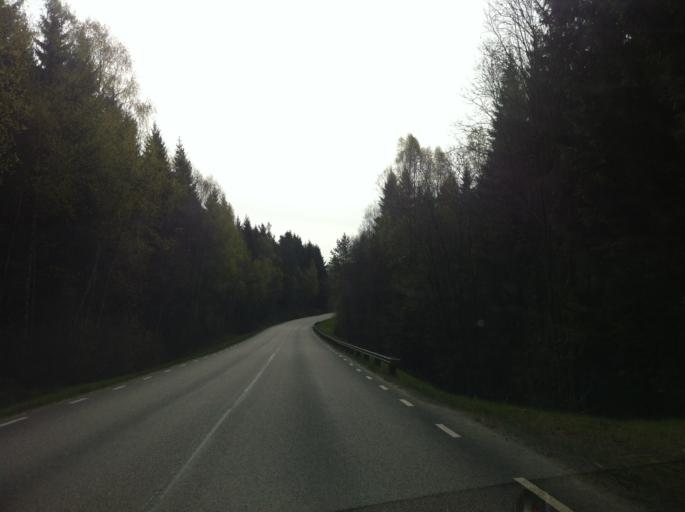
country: SE
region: Vaestra Goetaland
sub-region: Marks Kommun
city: Kinna
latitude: 57.4058
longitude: 12.7755
